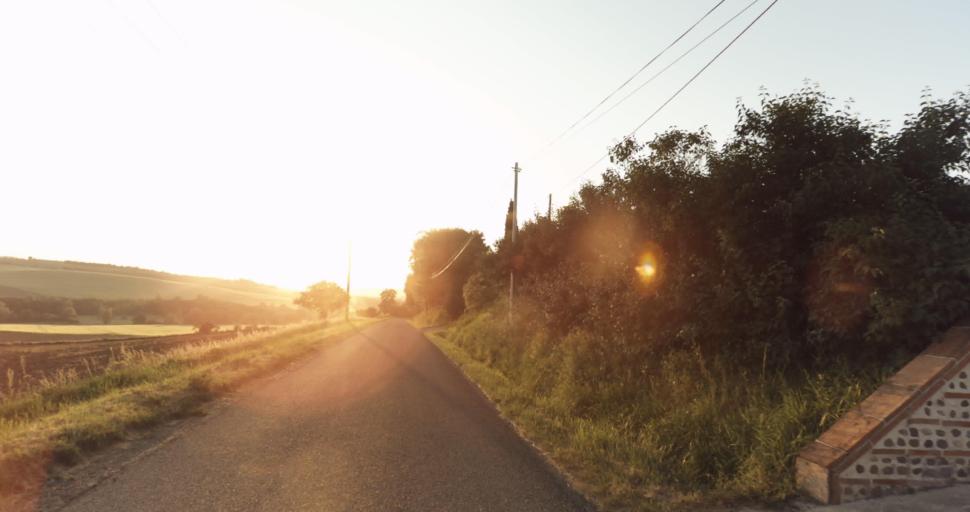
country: FR
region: Midi-Pyrenees
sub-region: Departement du Gers
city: Pujaudran
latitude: 43.6477
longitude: 1.1280
